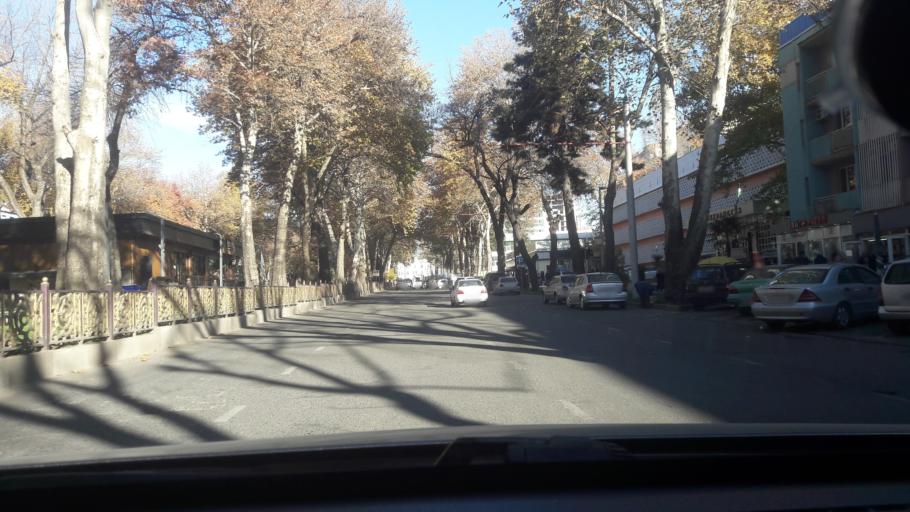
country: TJ
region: Dushanbe
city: Dushanbe
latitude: 38.5592
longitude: 68.7997
